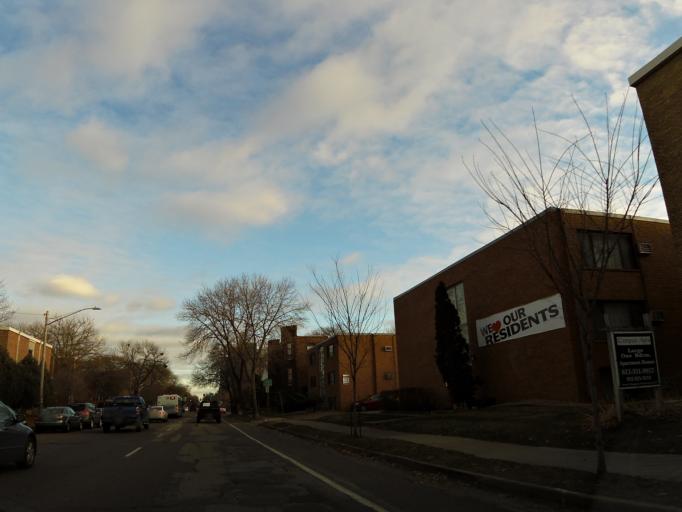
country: US
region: Minnesota
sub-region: Hennepin County
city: Minneapolis
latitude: 44.9833
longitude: -93.2461
